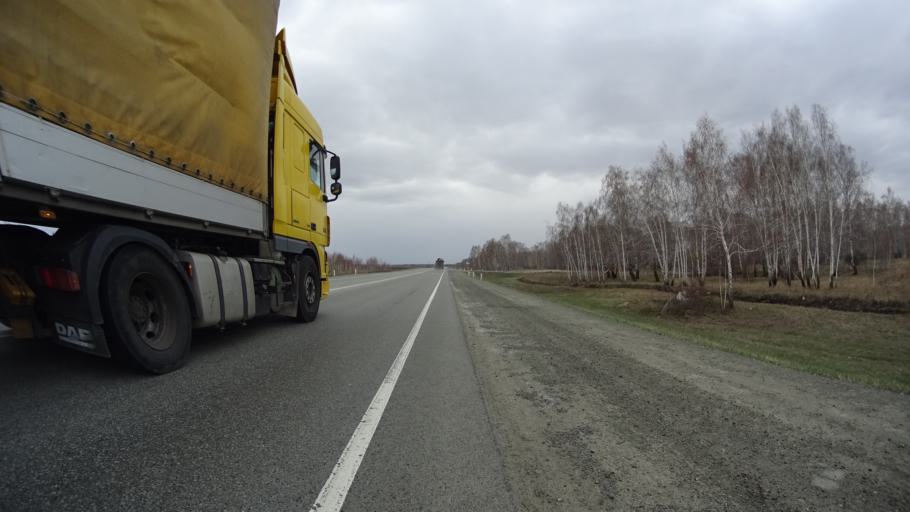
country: RU
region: Chelyabinsk
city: Krasnogorskiy
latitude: 54.6938
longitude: 61.2494
